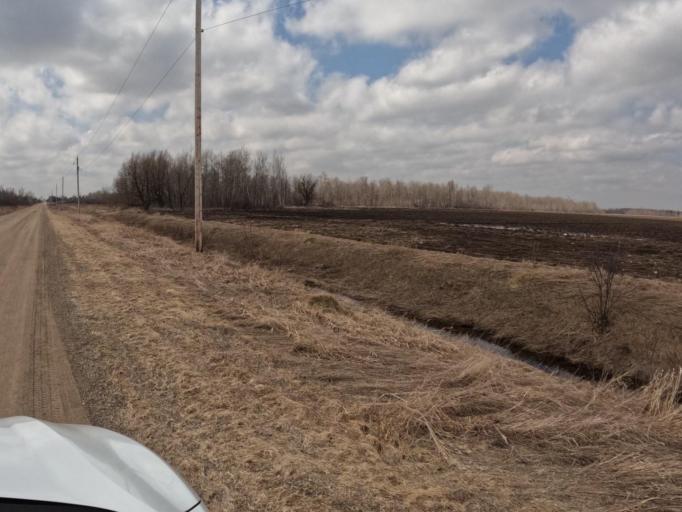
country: CA
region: Ontario
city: Shelburne
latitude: 44.0208
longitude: -80.2961
